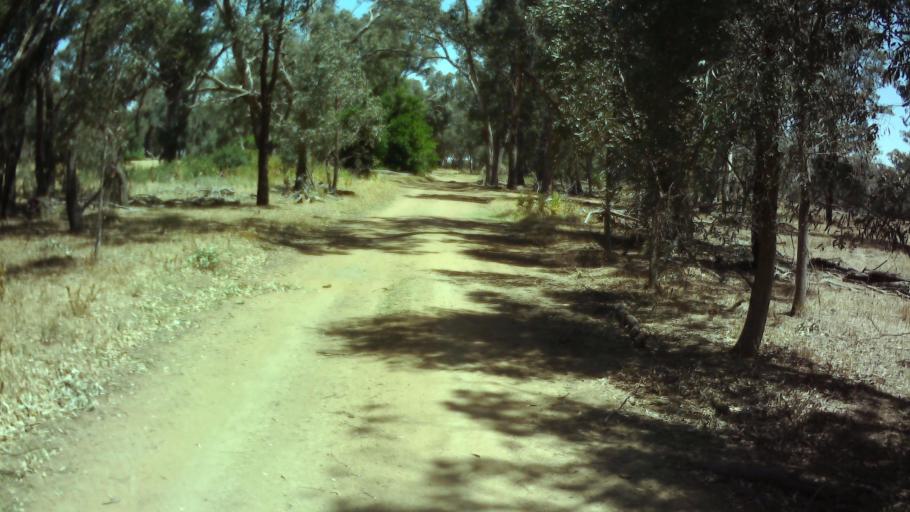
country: AU
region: New South Wales
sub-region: Weddin
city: Grenfell
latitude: -34.0455
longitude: 147.8380
